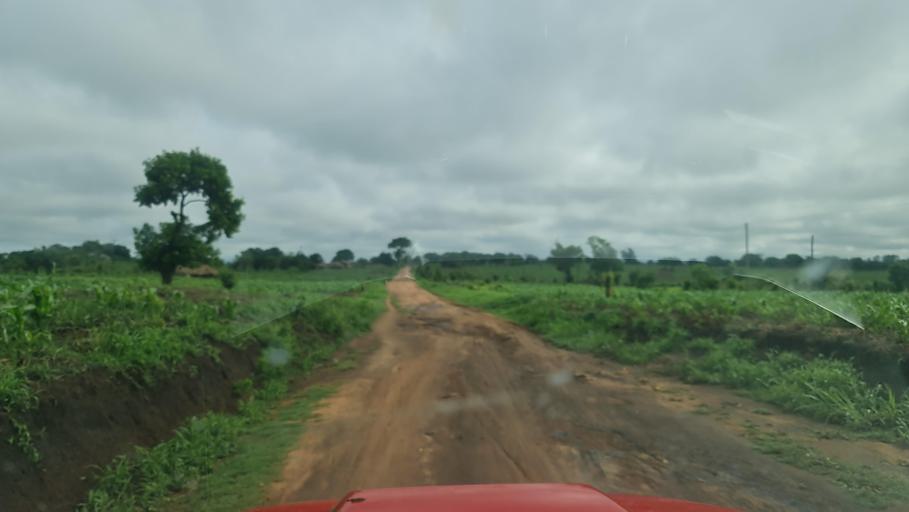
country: MW
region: Southern Region
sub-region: Nsanje District
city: Nsanje
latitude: -17.2081
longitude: 35.6804
